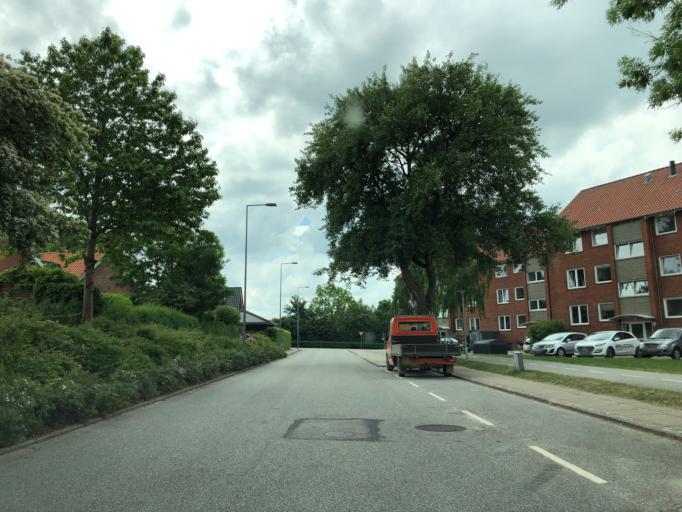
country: DK
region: Central Jutland
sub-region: Struer Kommune
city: Struer
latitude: 56.4881
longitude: 8.5903
